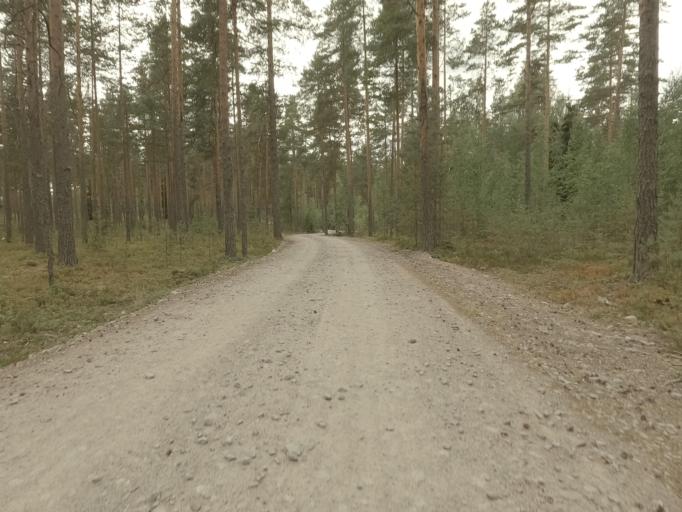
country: RU
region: Leningrad
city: Kamennogorsk
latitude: 60.9896
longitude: 29.1879
